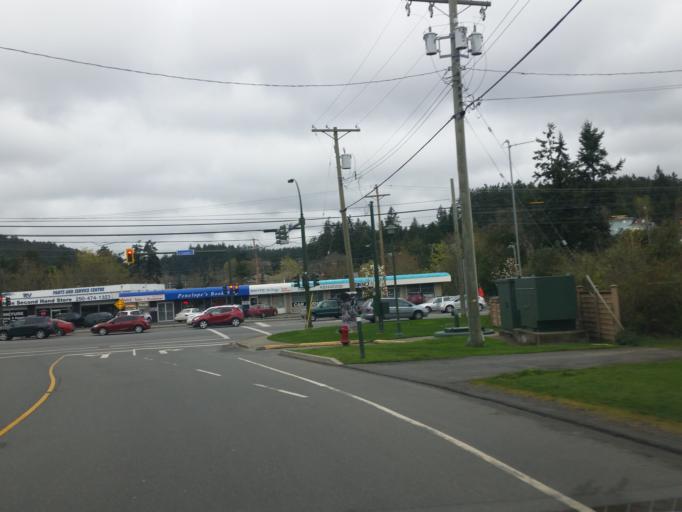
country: CA
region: British Columbia
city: Colwood
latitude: 48.4551
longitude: -123.4595
